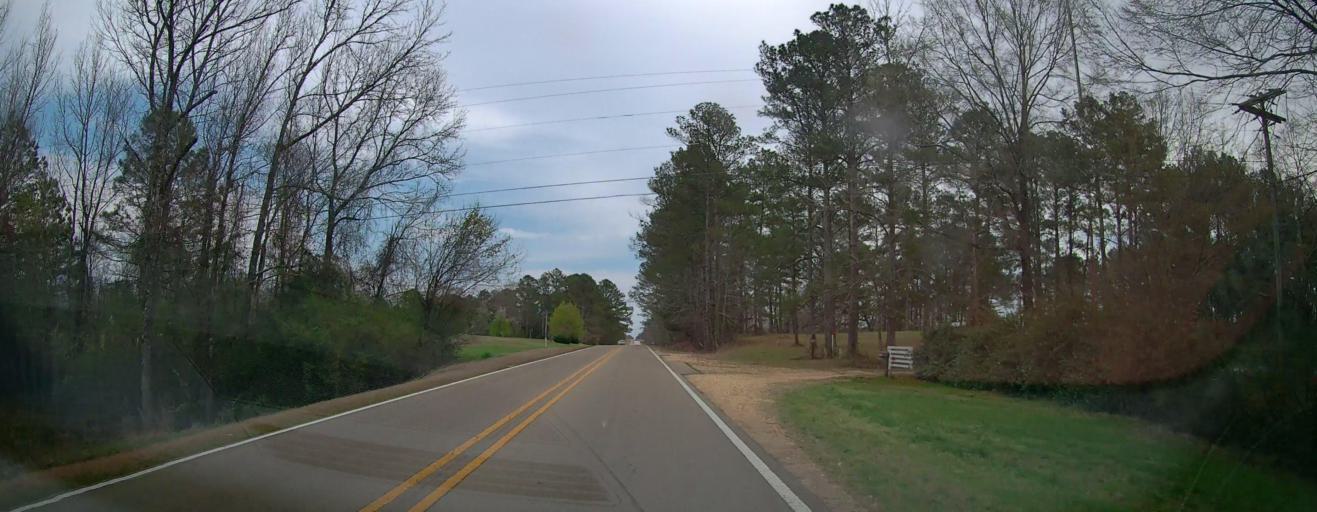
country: US
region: Mississippi
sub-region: Itawamba County
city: Mantachie
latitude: 34.2641
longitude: -88.5408
